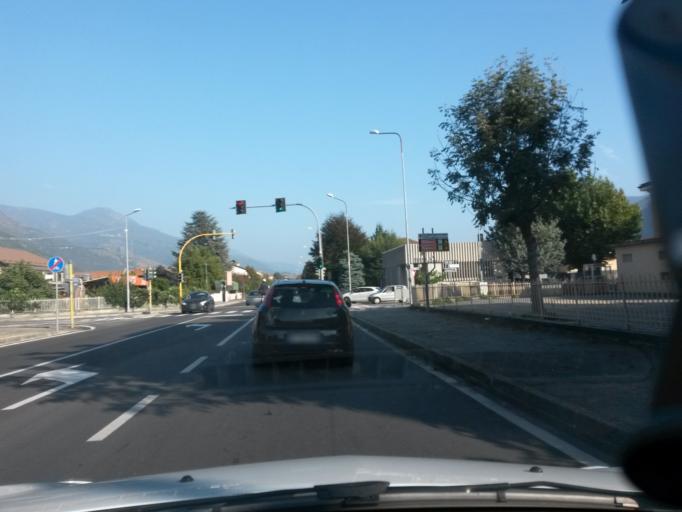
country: IT
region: Piedmont
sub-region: Provincia di Torino
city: Sant'Antonino di Susa
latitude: 45.1080
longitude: 7.2691
